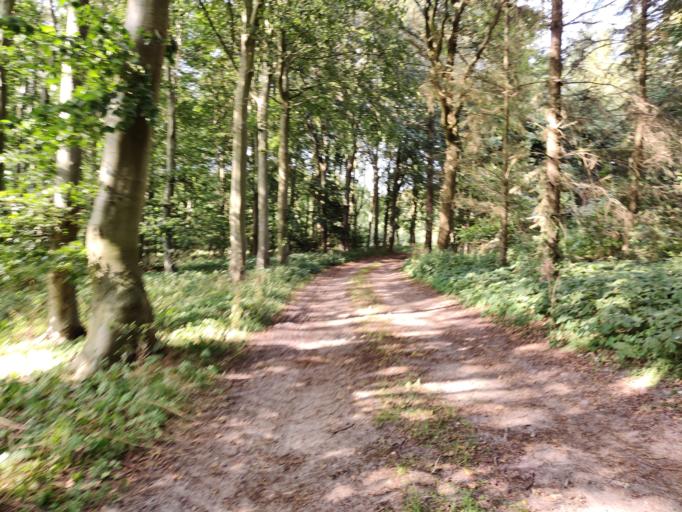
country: DK
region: Zealand
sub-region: Guldborgsund Kommune
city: Nykobing Falster
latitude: 54.6810
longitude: 11.9113
